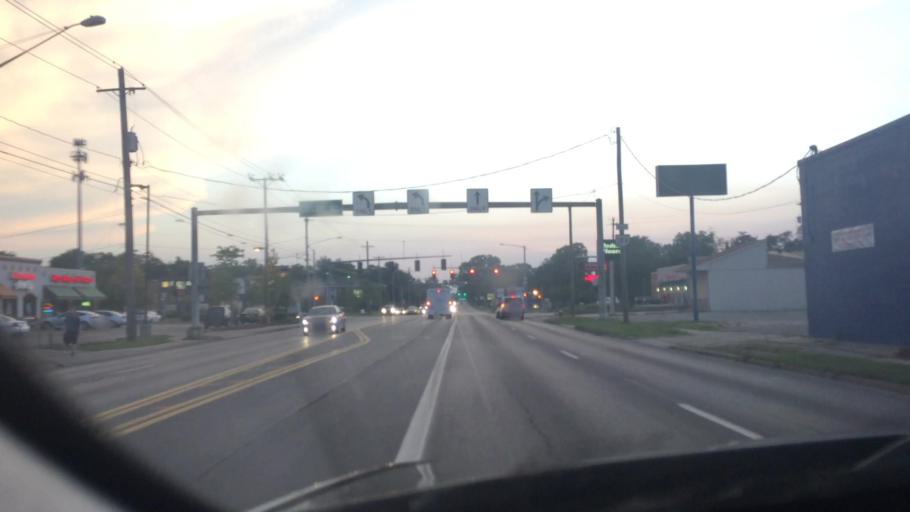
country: US
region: Michigan
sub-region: Monroe County
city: Lambertville
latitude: 41.7209
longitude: -83.6228
